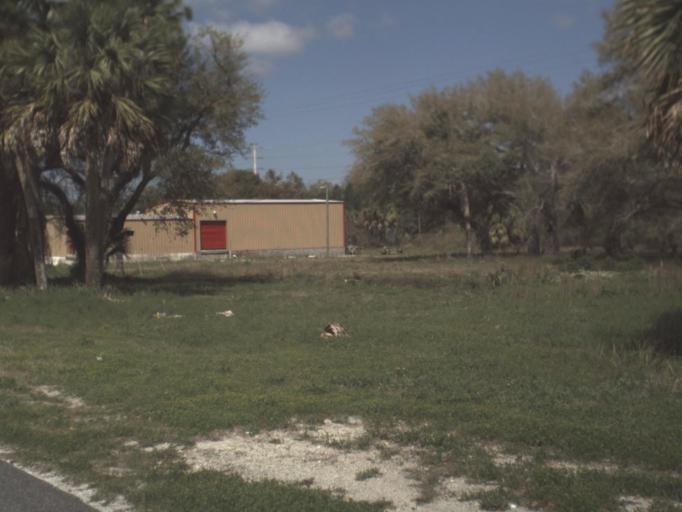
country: US
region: Florida
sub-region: Franklin County
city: Apalachicola
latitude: 29.7140
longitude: -85.0180
